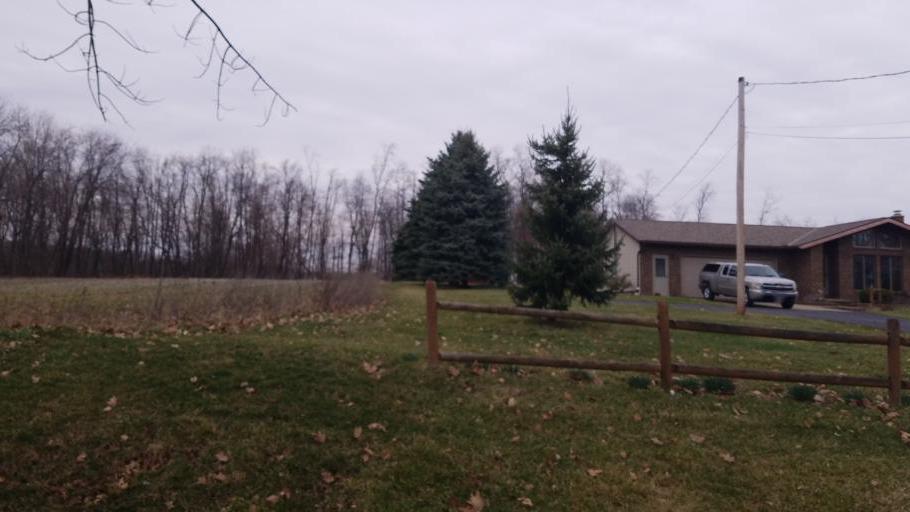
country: US
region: Ohio
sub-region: Sandusky County
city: Bellville
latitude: 40.6817
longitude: -82.4771
